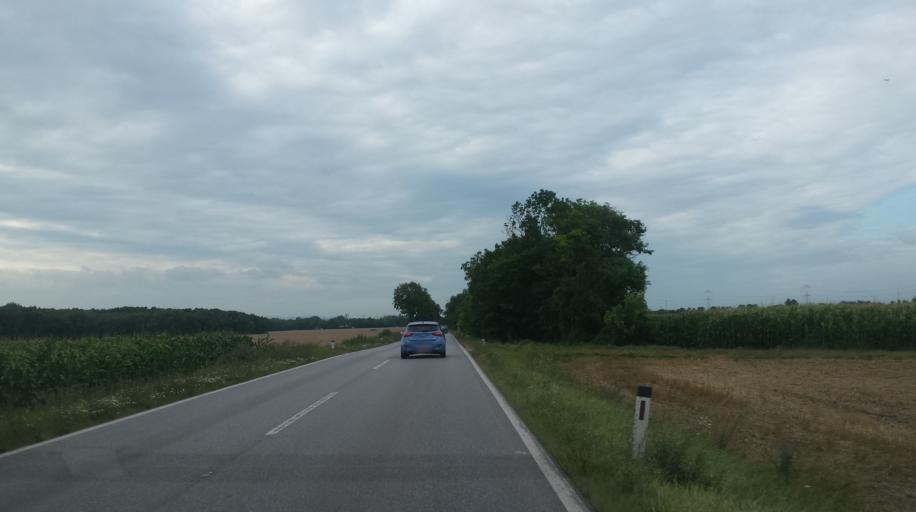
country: AT
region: Lower Austria
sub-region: Politischer Bezirk Wien-Umgebung
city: Moosbrunn
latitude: 48.0493
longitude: 16.4619
